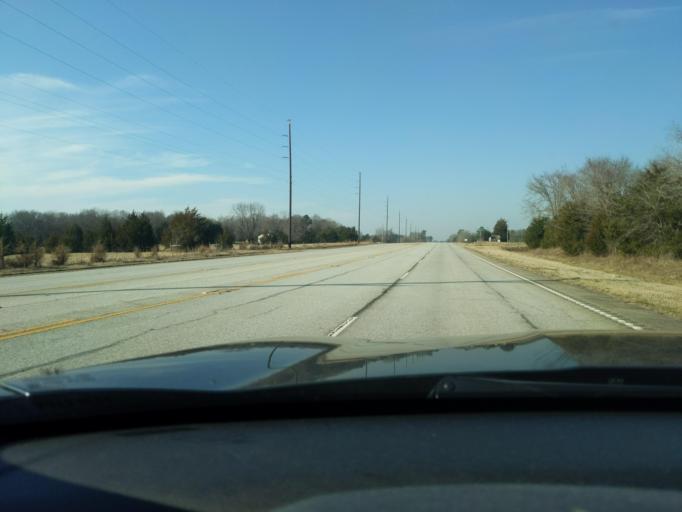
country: US
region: South Carolina
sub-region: Abbeville County
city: Calhoun Falls
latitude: 34.1019
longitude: -82.5444
